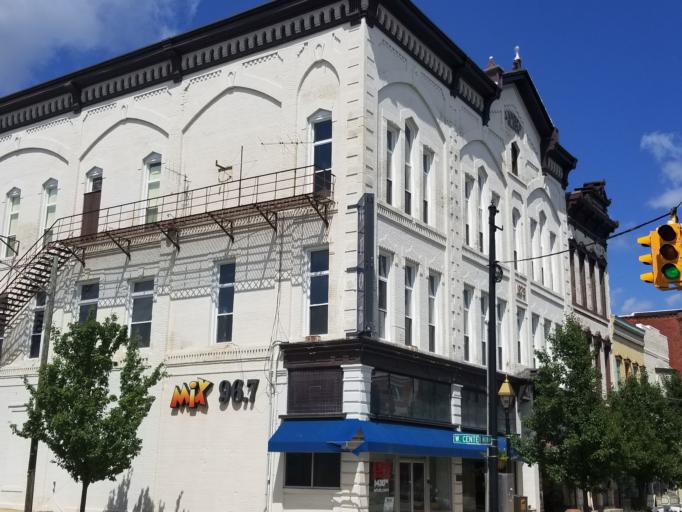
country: US
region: Ohio
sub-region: Seneca County
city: Fostoria
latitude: 41.1576
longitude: -83.4141
